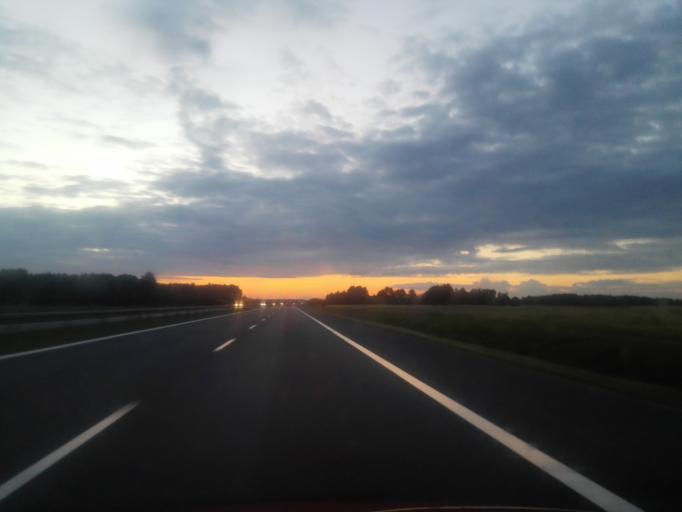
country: PL
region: Lodz Voivodeship
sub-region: Powiat piotrkowski
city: Grabica
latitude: 51.4854
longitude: 19.6191
